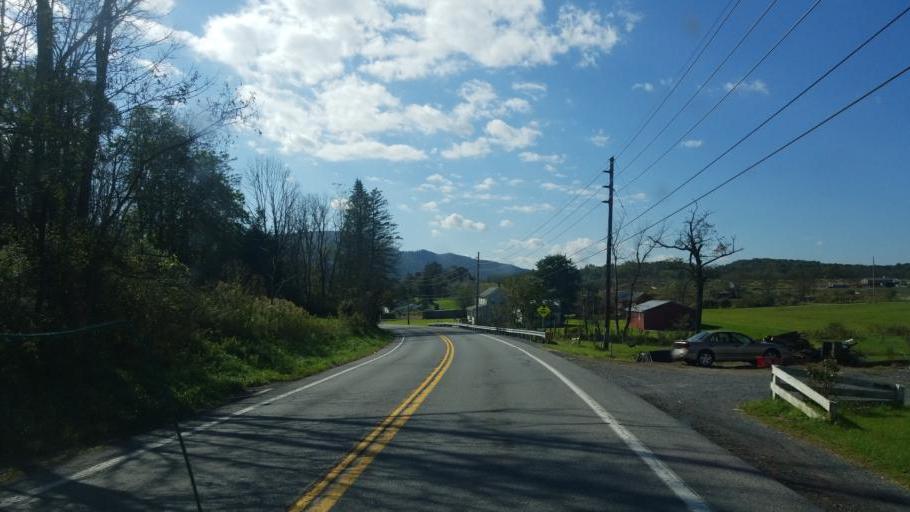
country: US
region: Pennsylvania
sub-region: Bedford County
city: Bedford
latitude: 40.0574
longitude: -78.5535
